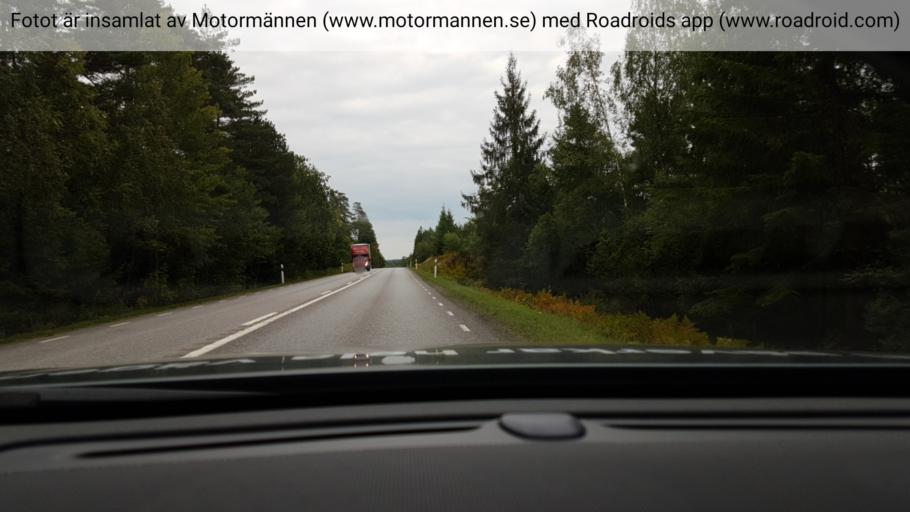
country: SE
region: Joenkoeping
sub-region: Gislaveds Kommun
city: Reftele
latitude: 57.1571
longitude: 13.5141
